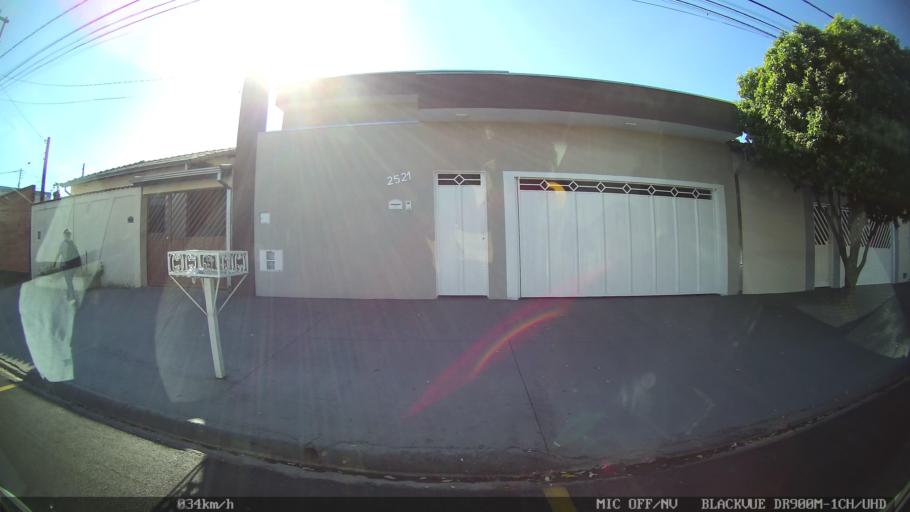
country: BR
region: Sao Paulo
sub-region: Franca
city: Franca
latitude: -20.5100
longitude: -47.4183
